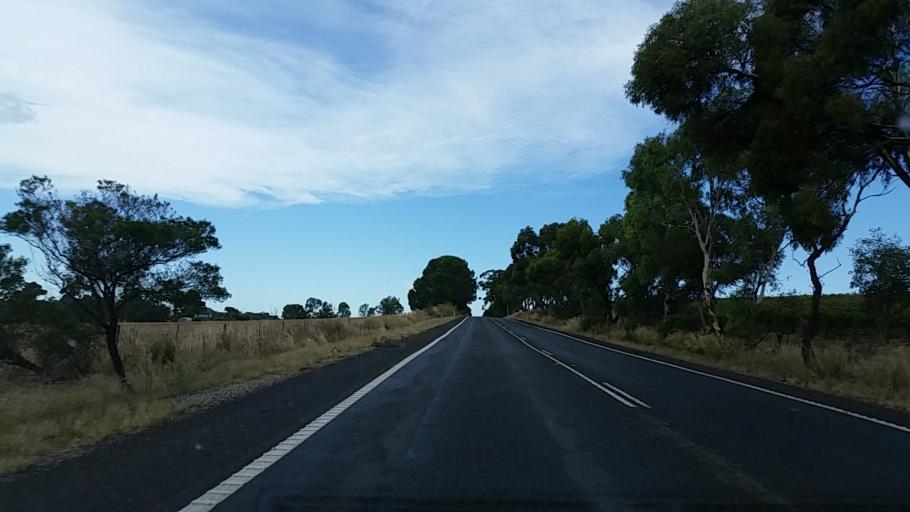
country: AU
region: South Australia
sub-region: Barossa
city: Tanunda
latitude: -34.5353
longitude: 138.9156
